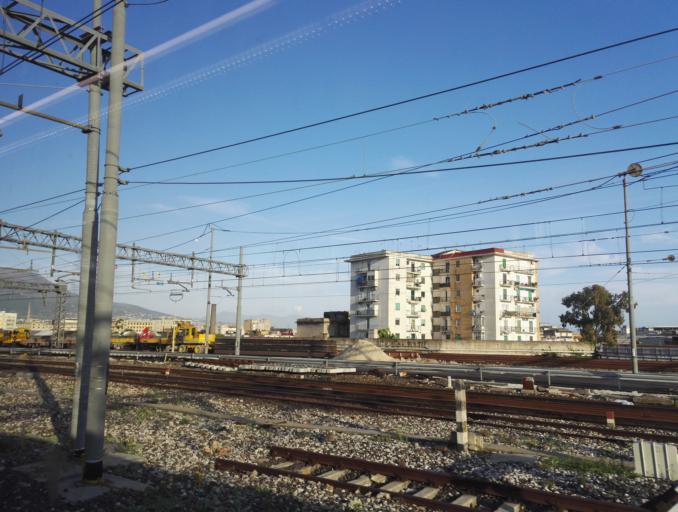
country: IT
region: Campania
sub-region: Provincia di Napoli
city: Napoli
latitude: 40.8535
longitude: 14.2830
